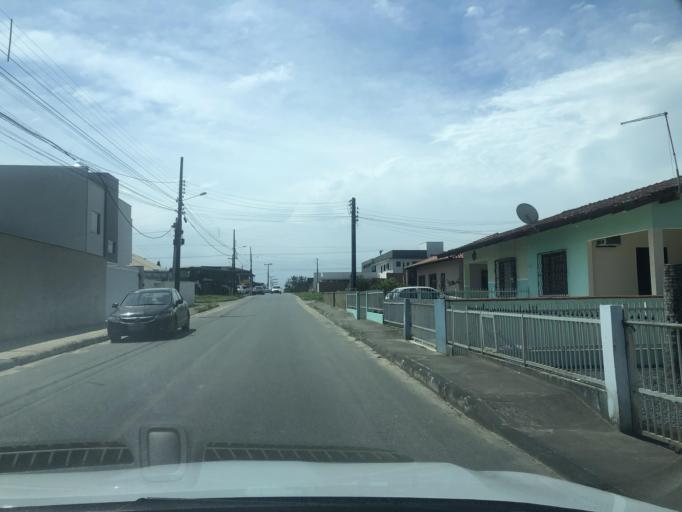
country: BR
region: Santa Catarina
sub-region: Sao Francisco Do Sul
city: Sao Francisco do Sul
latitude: -26.2081
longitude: -48.5400
